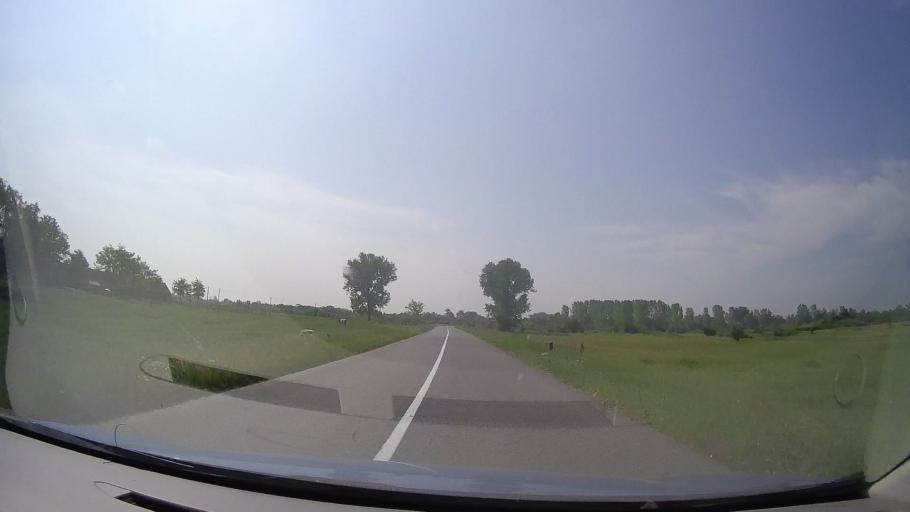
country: RS
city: Jarkovac
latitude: 45.2775
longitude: 20.7631
